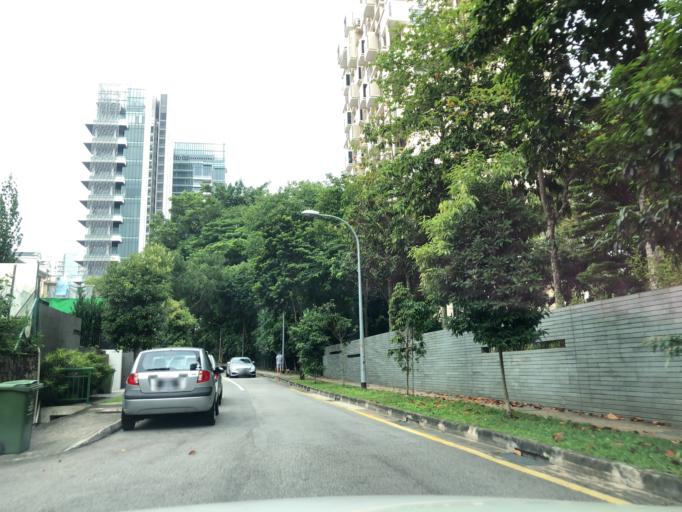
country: SG
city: Singapore
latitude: 1.3004
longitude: 103.8263
